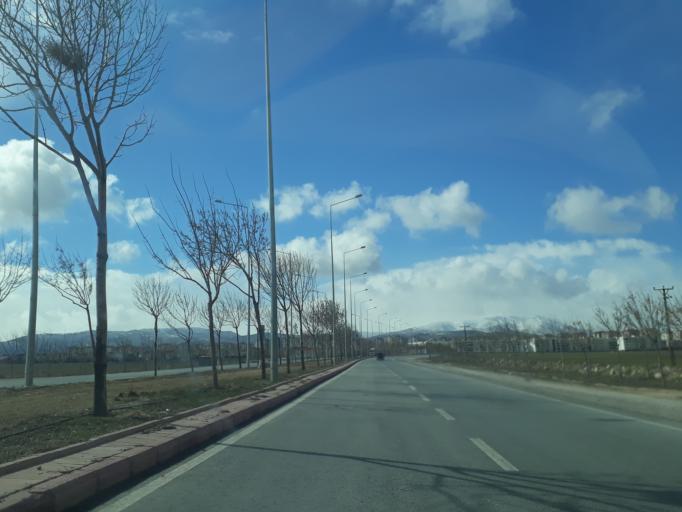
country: TR
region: Konya
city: Asagipinarbasi
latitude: 38.0052
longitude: 32.5485
